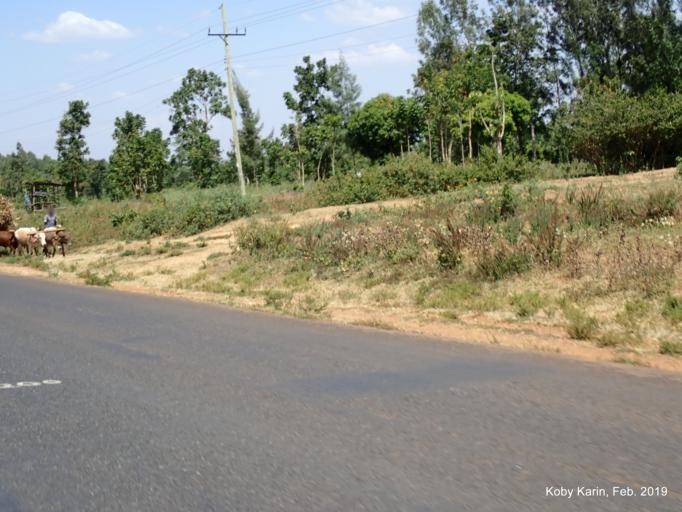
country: KE
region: Kakamega
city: Butere
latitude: 0.1290
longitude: 34.4274
